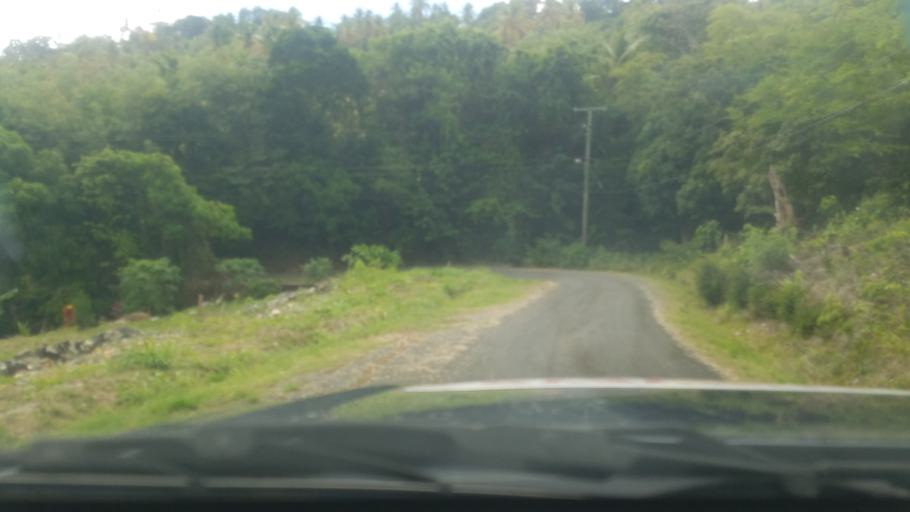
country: LC
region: Praslin
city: Praslin
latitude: 13.8629
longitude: -60.9053
